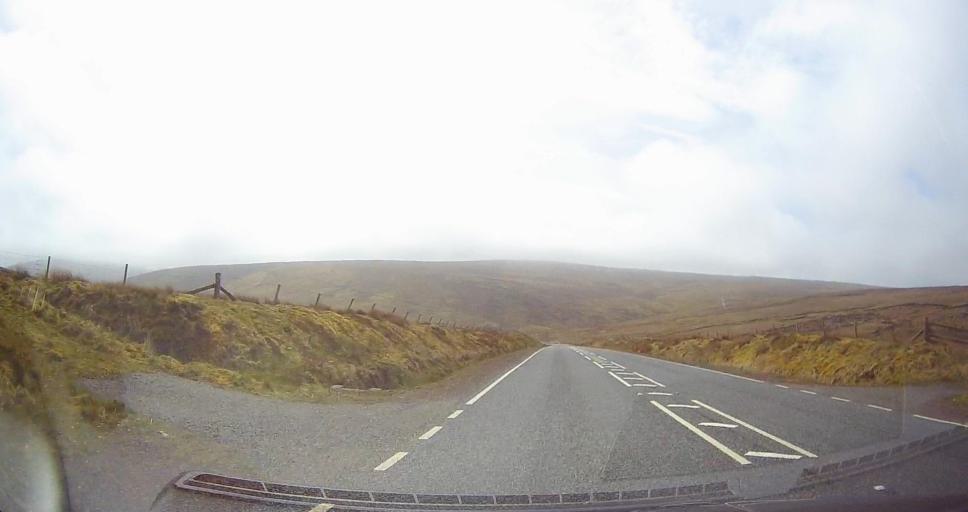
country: GB
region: Scotland
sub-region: Shetland Islands
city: Sandwick
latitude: 60.0079
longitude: -1.2709
